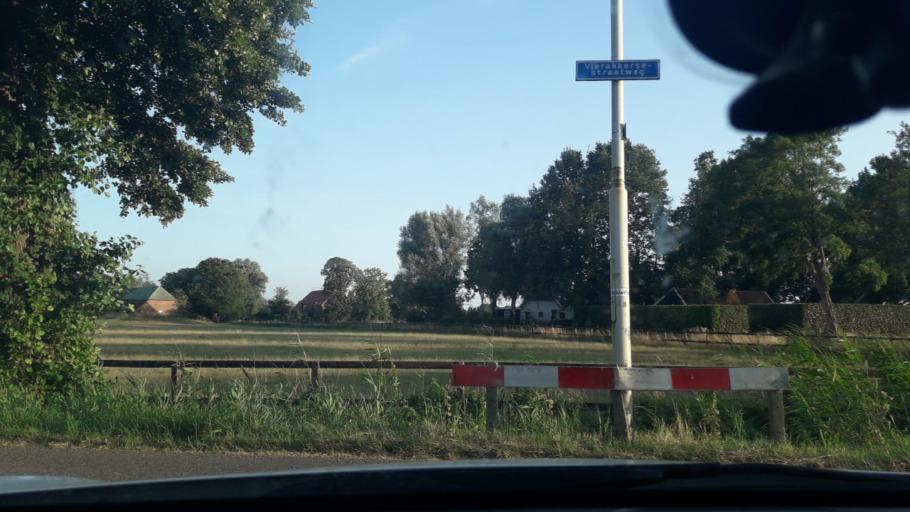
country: NL
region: Gelderland
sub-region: Gemeente Zutphen
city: Leesten
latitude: 52.1073
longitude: 6.2385
